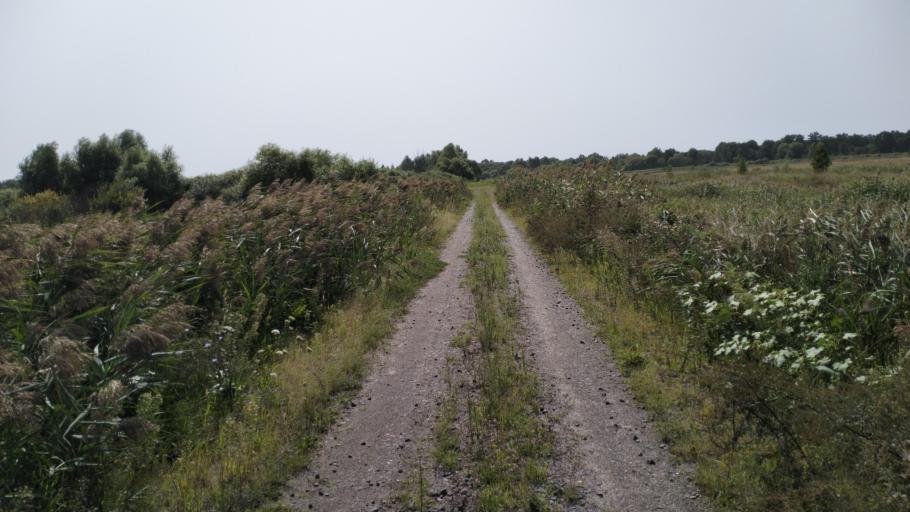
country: BY
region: Brest
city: Davyd-Haradok
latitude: 51.9689
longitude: 27.1736
